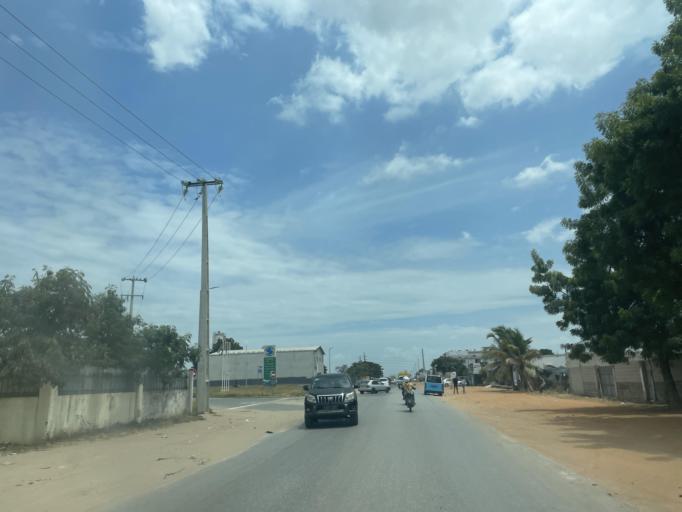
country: AO
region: Luanda
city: Luanda
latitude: -8.9342
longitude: 13.3818
